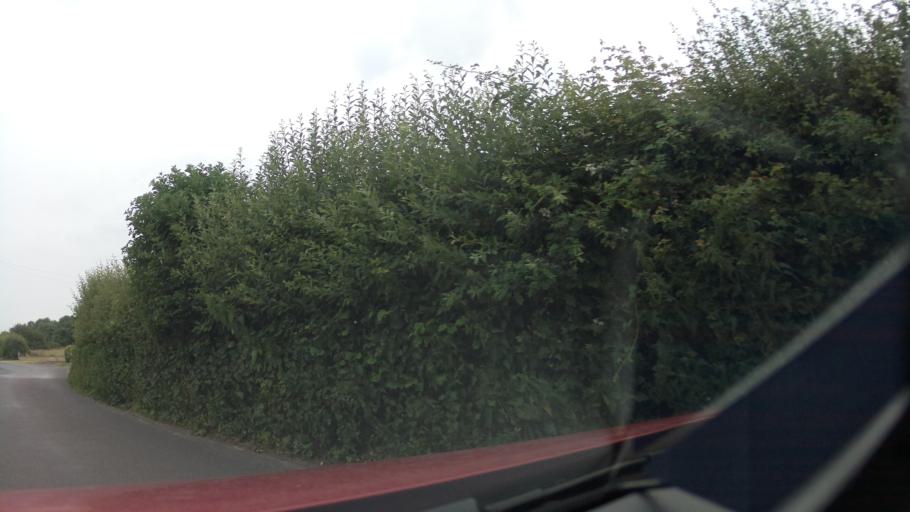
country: GB
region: England
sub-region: Somerset
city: Yeovil
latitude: 50.9790
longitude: -2.6002
